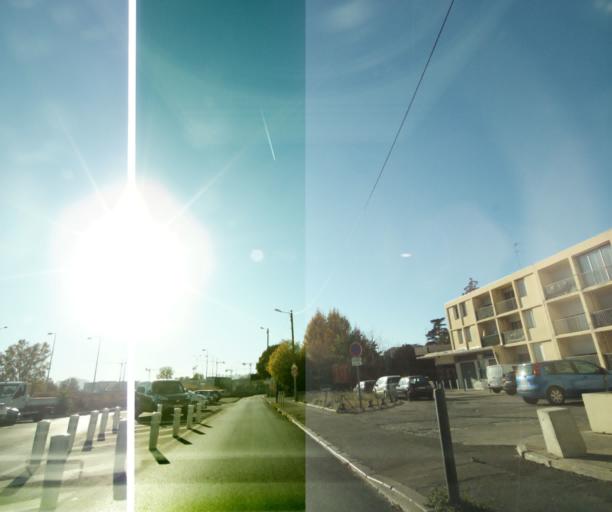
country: FR
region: Provence-Alpes-Cote d'Azur
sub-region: Departement des Bouches-du-Rhone
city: Marseille 11
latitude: 43.2869
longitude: 5.4317
